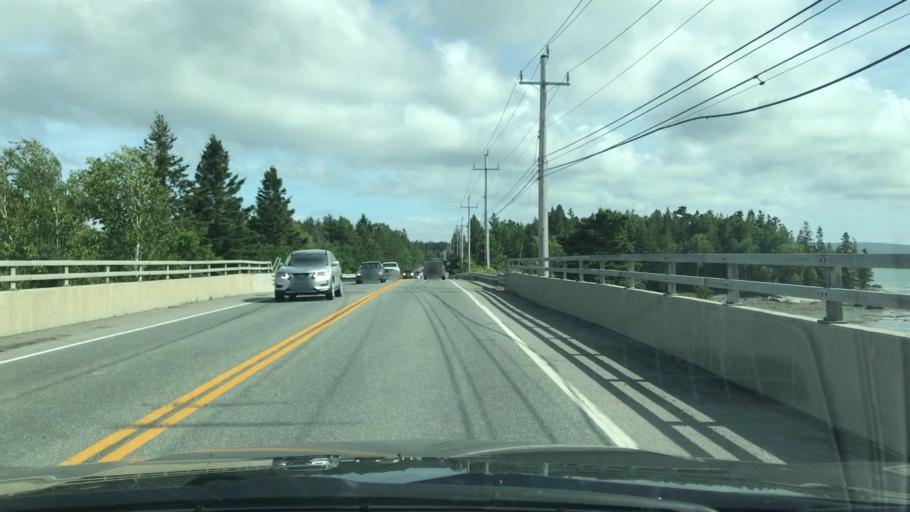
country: US
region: Maine
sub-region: Hancock County
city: Trenton
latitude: 44.4301
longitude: -68.3676
